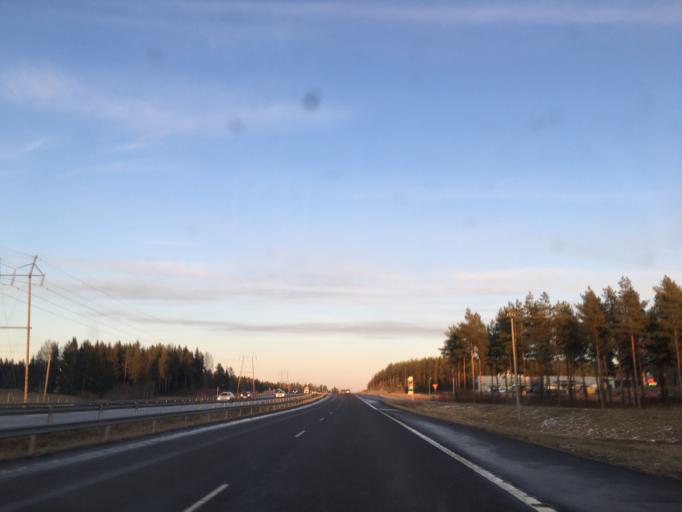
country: FI
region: Varsinais-Suomi
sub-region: Turku
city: Vahto
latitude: 60.5426
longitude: 22.3377
